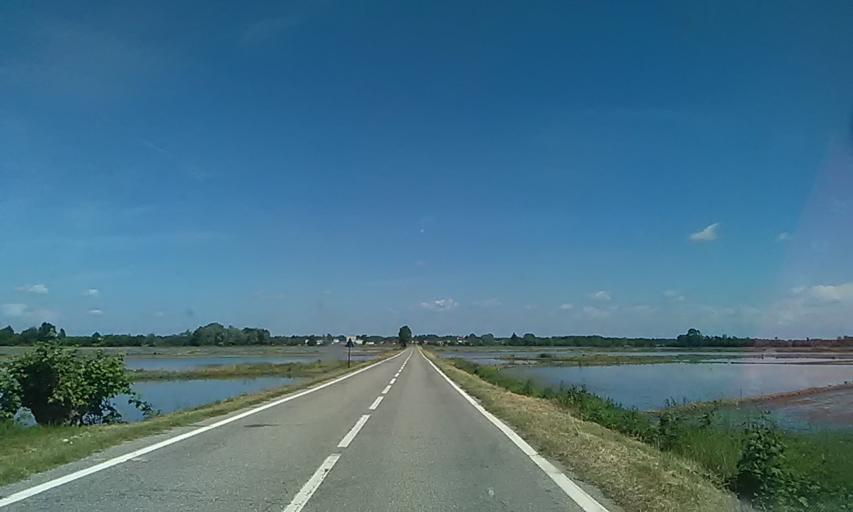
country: IT
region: Piedmont
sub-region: Provincia di Vercelli
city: Villarboit
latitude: 45.4322
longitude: 8.3581
